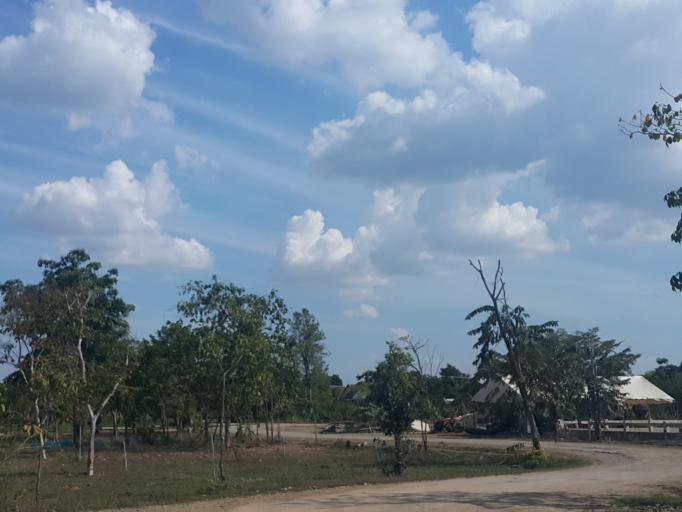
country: TH
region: Sukhothai
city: Si Samrong
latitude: 17.2283
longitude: 99.8210
